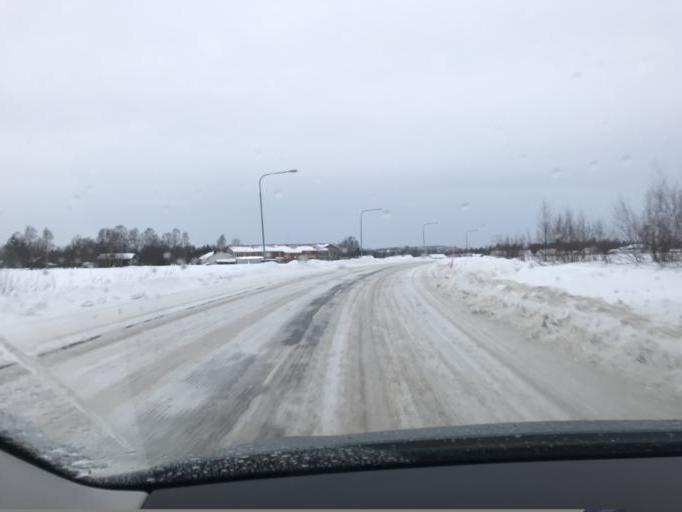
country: SE
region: Norrbotten
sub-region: Lulea Kommun
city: Sodra Sunderbyn
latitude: 65.6652
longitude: 21.9339
